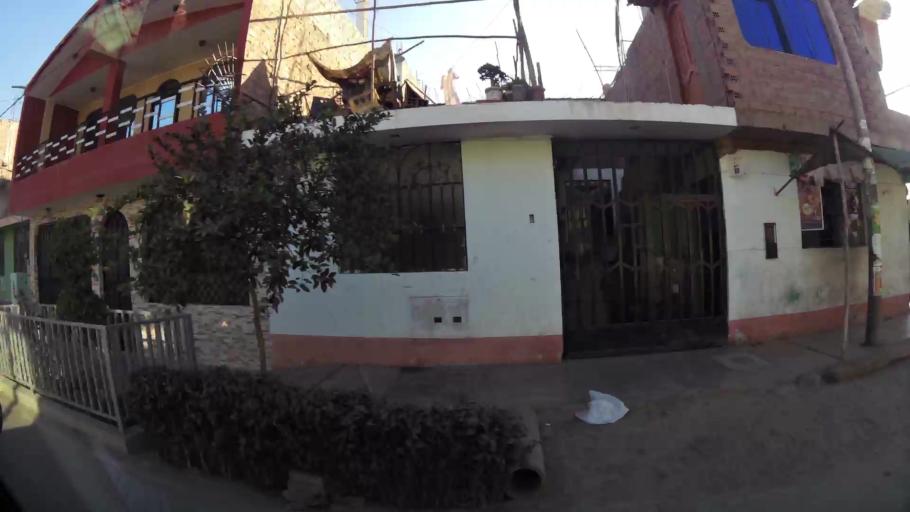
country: PE
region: Ica
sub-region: Provincia de Ica
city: Ica
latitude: -14.0693
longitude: -75.7179
